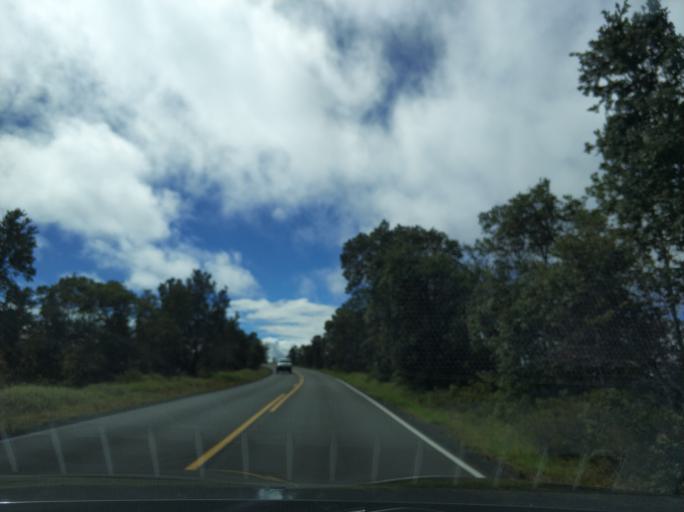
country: US
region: Hawaii
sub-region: Hawaii County
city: Volcano
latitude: 19.4250
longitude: -155.2871
